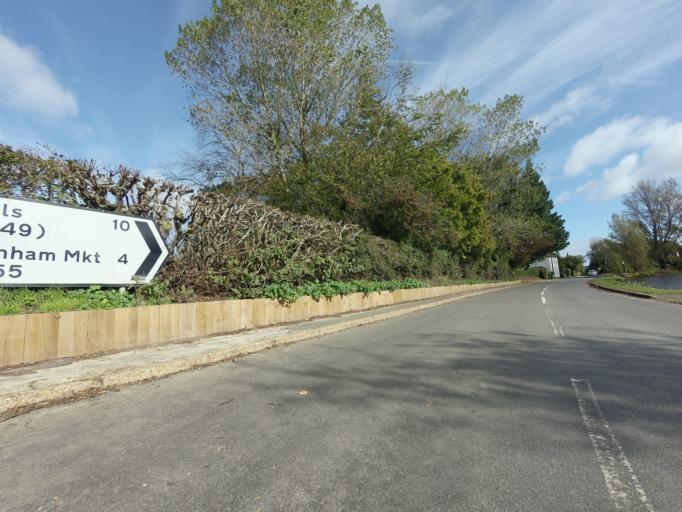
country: GB
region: England
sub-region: Norfolk
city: Wells-next-the-Sea
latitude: 52.9011
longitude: 0.6842
